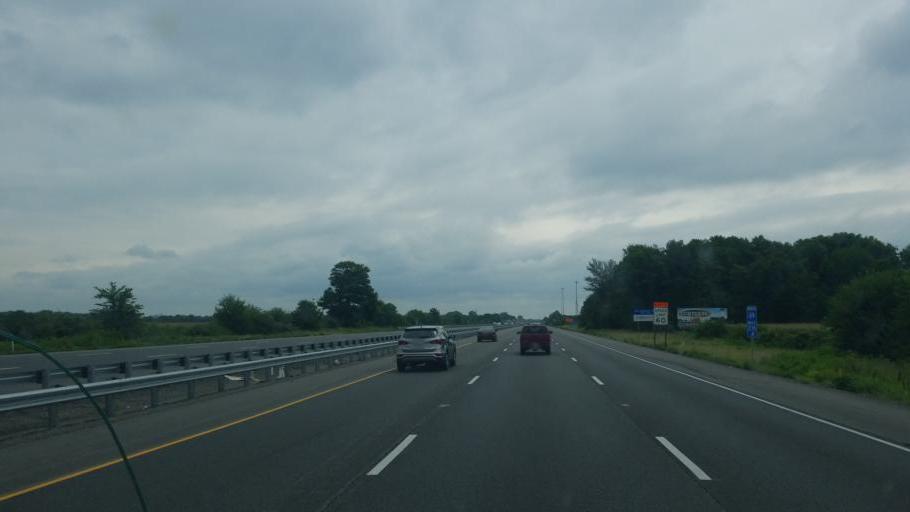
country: US
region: Indiana
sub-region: Madison County
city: Ingalls
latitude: 39.9914
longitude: -85.8072
